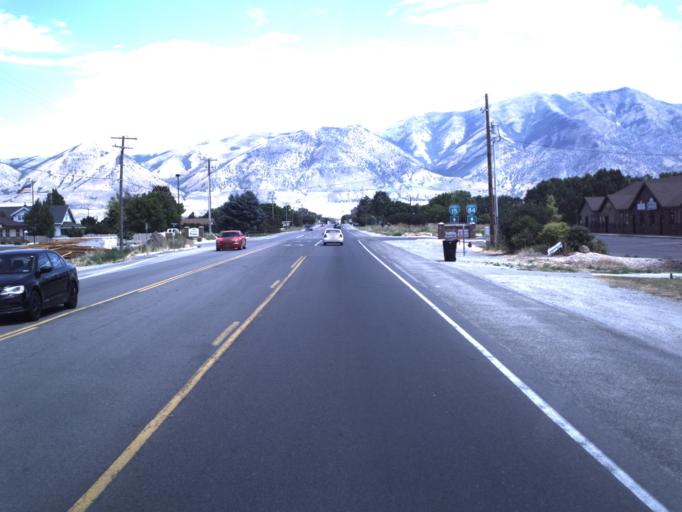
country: US
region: Utah
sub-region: Box Elder County
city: Tremonton
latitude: 41.7120
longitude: -112.1551
